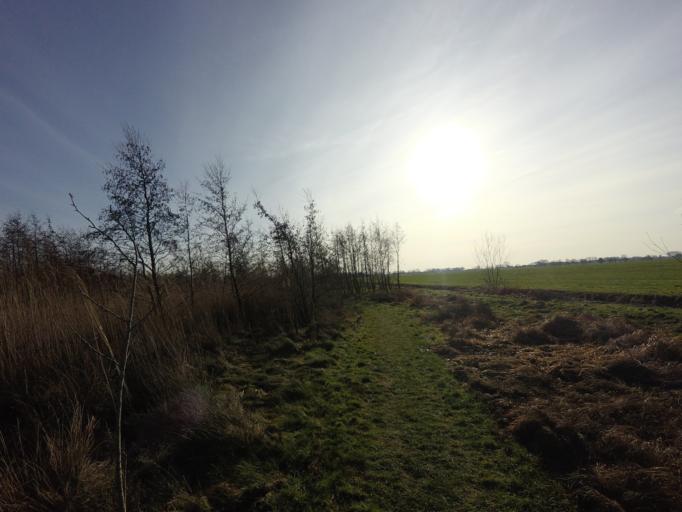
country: NL
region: Utrecht
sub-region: Gemeente Oudewater
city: Oudewater
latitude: 52.0331
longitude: 4.8554
